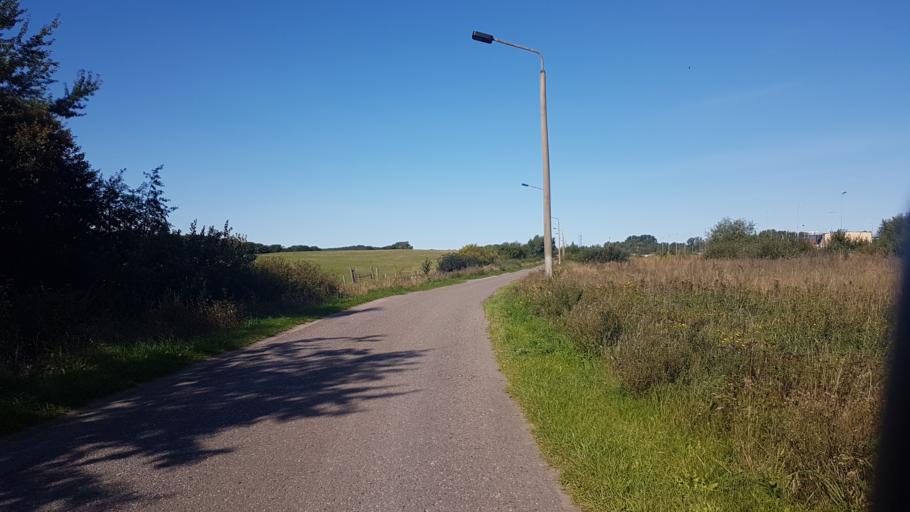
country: DE
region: Mecklenburg-Vorpommern
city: Sagard
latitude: 54.4969
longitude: 13.5479
